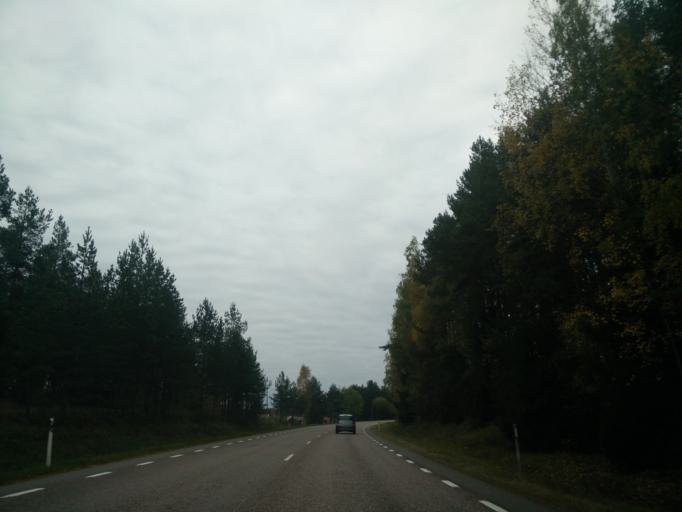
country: SE
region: Gaevleborg
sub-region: Gavle Kommun
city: Norrsundet
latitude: 60.8268
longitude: 17.2117
